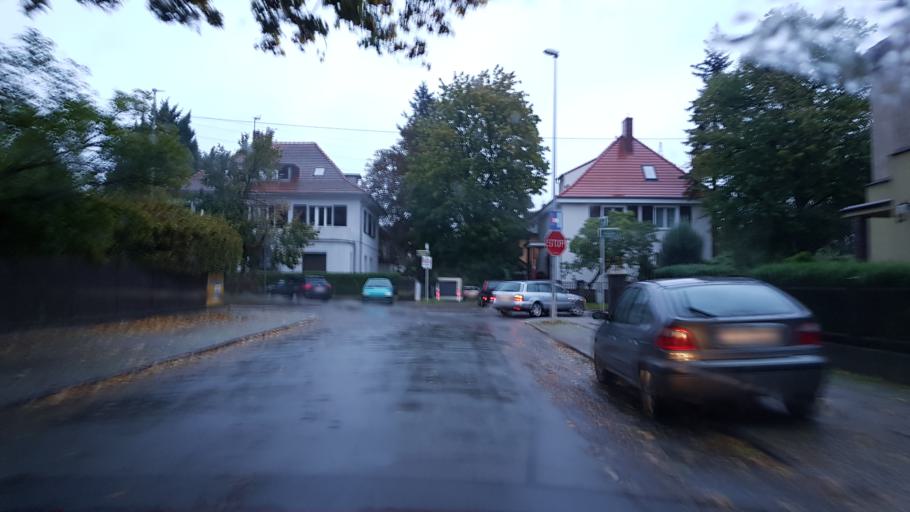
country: PL
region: West Pomeranian Voivodeship
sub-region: Szczecin
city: Szczecin
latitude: 53.4465
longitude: 14.5193
